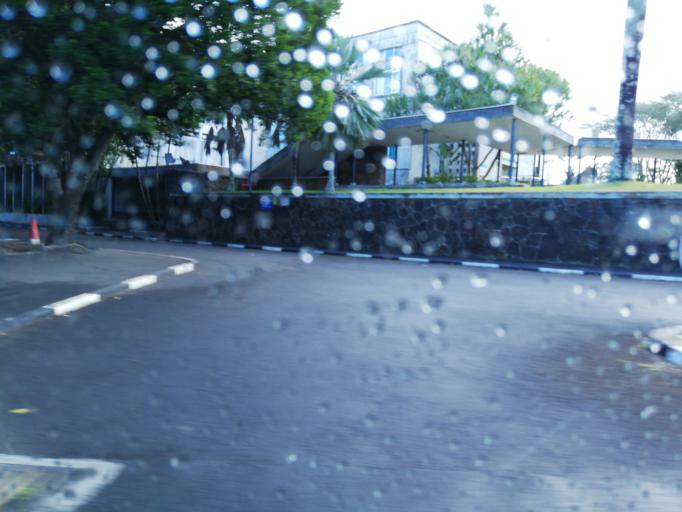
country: MU
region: Plaines Wilhems
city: Ebene
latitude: -20.2341
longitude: 57.4970
